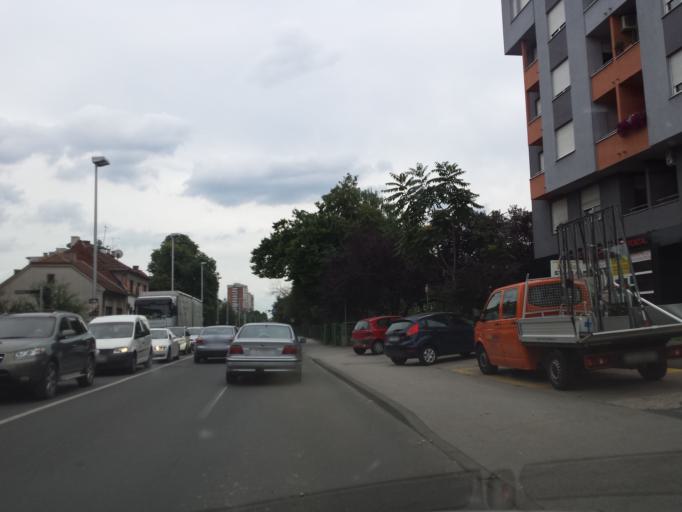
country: HR
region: Grad Zagreb
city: Zagreb - Centar
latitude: 45.7971
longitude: 15.9434
